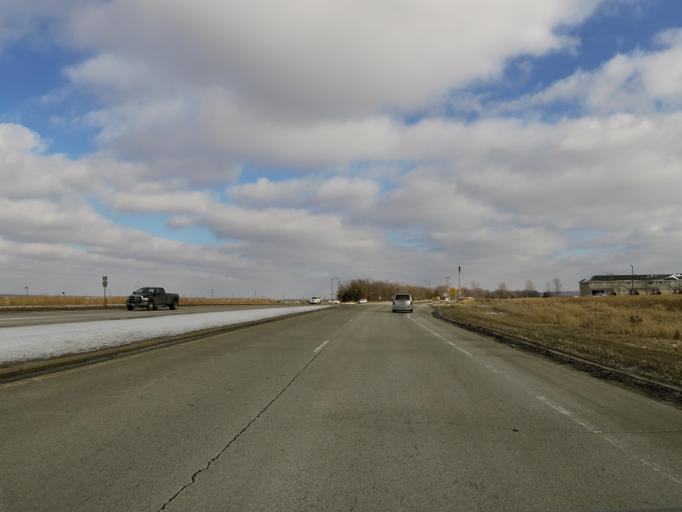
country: US
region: Minnesota
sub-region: Scott County
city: Shakopee
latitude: 44.7756
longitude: -93.4673
